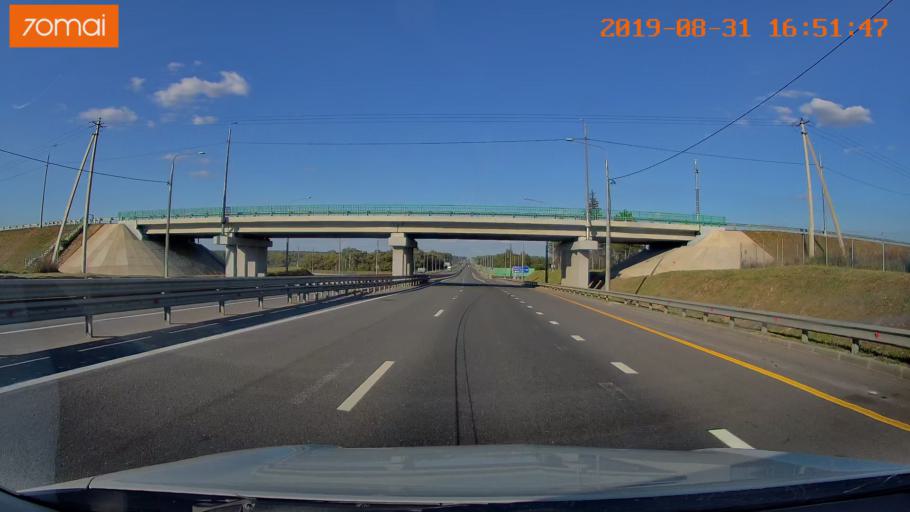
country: RU
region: Kaluga
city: Pyatovskiy
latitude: 54.7318
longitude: 36.1779
